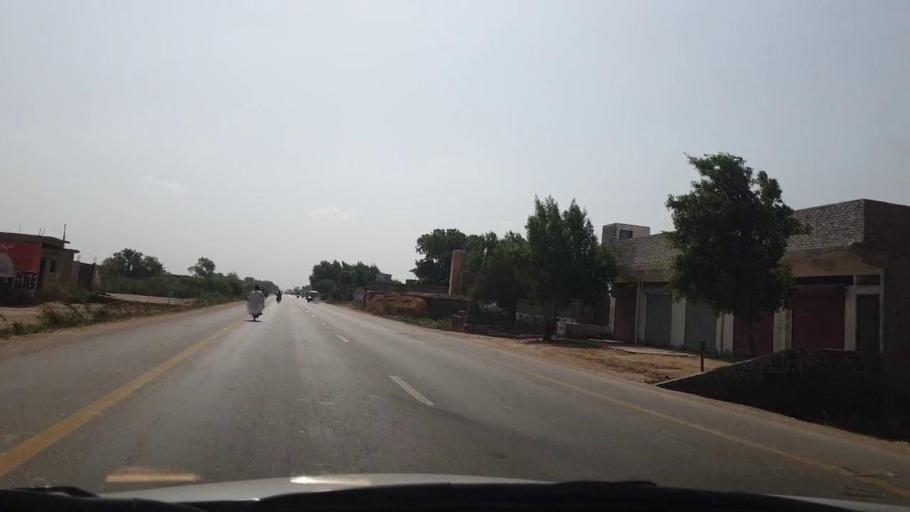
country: PK
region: Sindh
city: Matli
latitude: 25.0683
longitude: 68.6264
